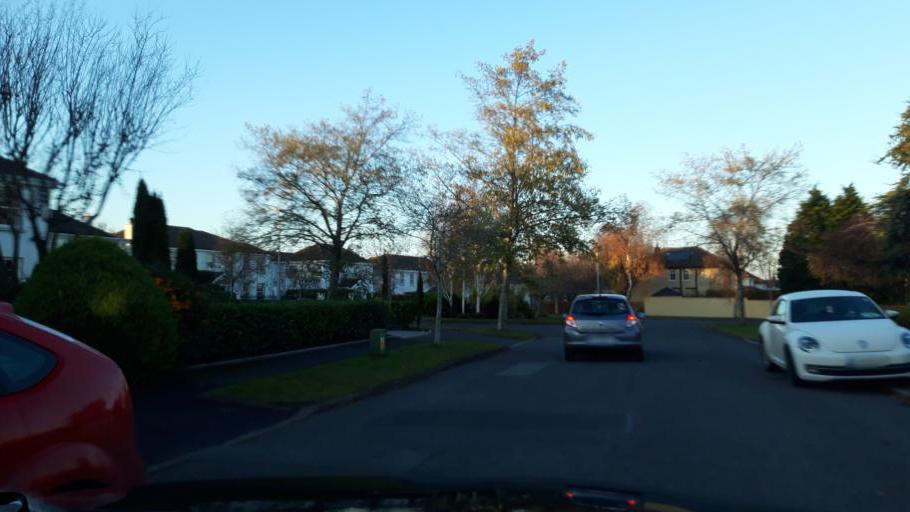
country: IE
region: Leinster
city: Castleknock
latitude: 53.3697
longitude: -6.3588
